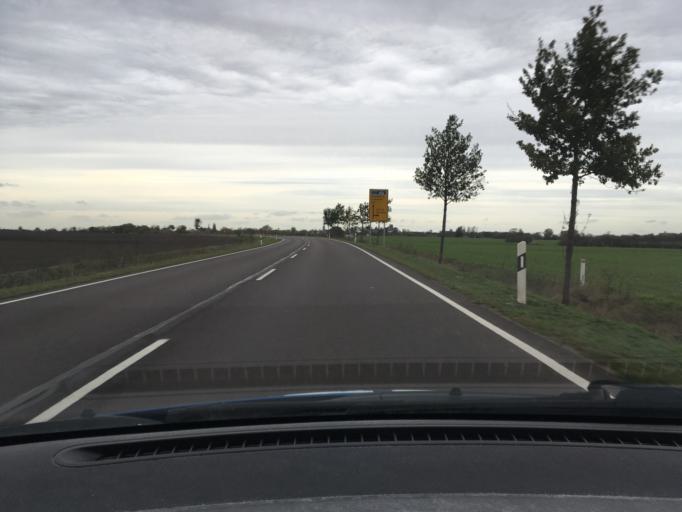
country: DE
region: Saxony-Anhalt
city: Leitzkau
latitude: 52.0458
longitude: 11.9709
